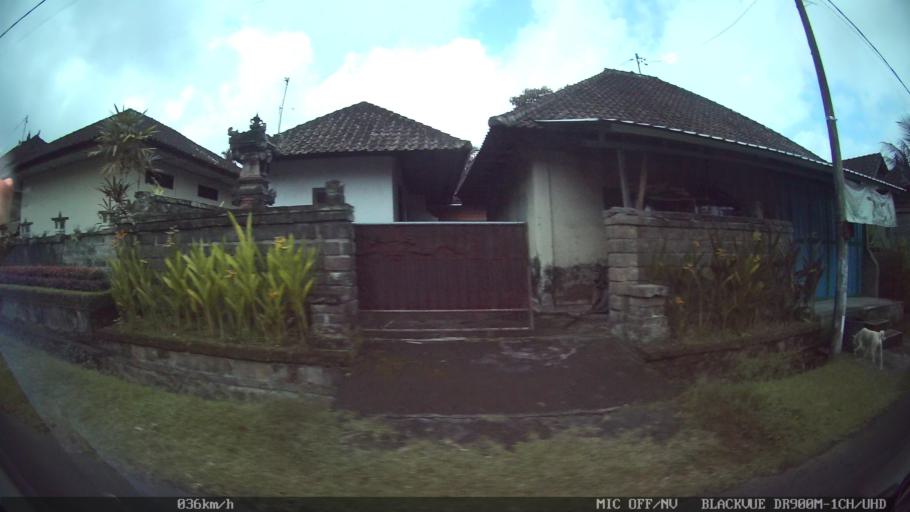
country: ID
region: Bali
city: Badung
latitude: -8.4273
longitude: 115.2261
